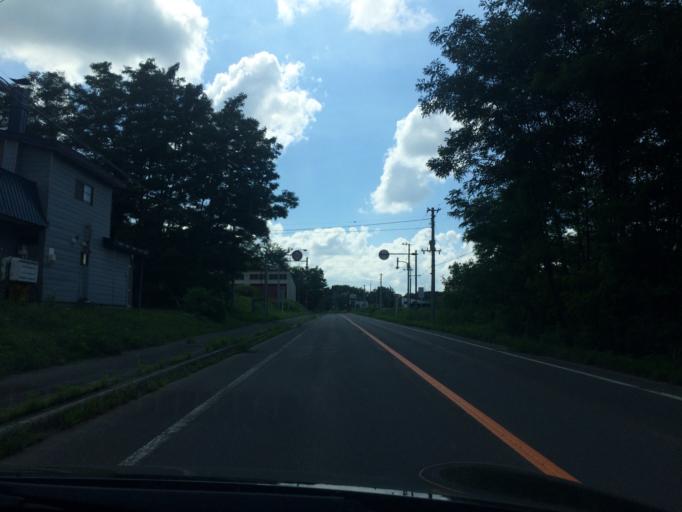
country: JP
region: Hokkaido
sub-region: Asahikawa-shi
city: Asahikawa
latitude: 43.7733
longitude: 142.4826
